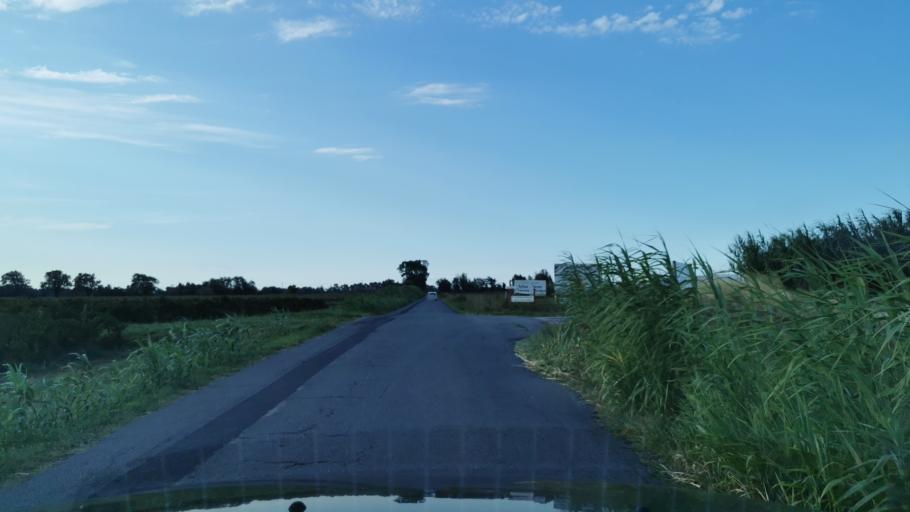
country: FR
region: Languedoc-Roussillon
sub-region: Departement de l'Aude
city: Narbonne
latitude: 43.1347
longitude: 3.0252
